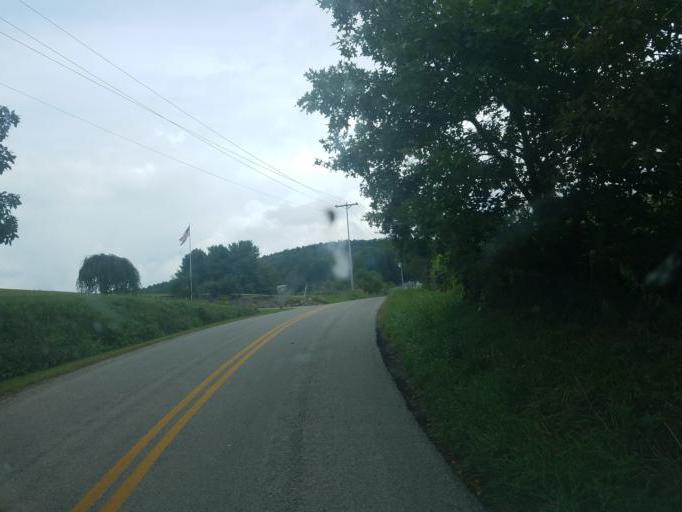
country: US
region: Ohio
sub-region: Ashland County
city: Loudonville
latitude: 40.5654
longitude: -82.3073
